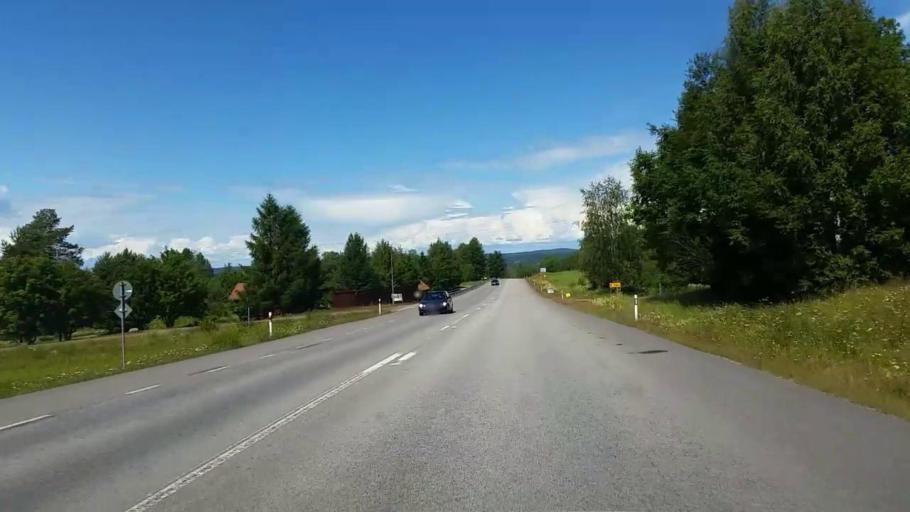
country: SE
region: Dalarna
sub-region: Rattviks Kommun
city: Raettvik
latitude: 60.8505
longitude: 15.1050
